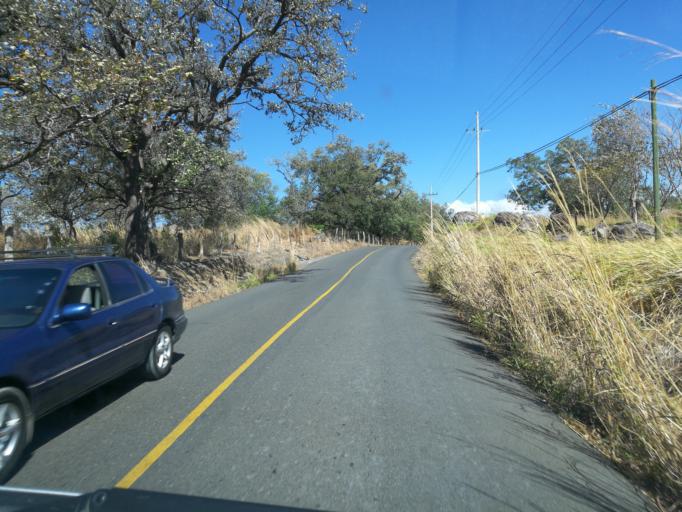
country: CR
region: Guanacaste
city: Liberia
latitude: 10.6663
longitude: -85.4657
